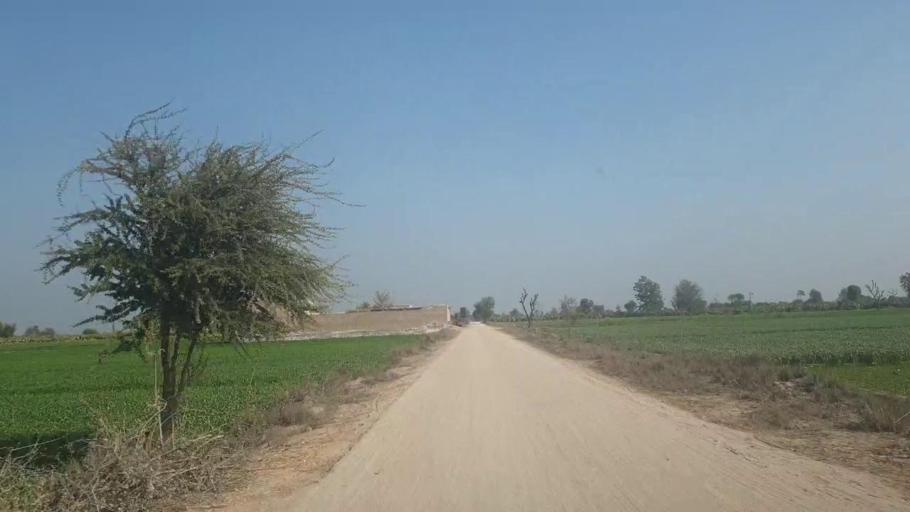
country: PK
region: Sindh
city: Sakrand
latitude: 26.0732
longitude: 68.4186
